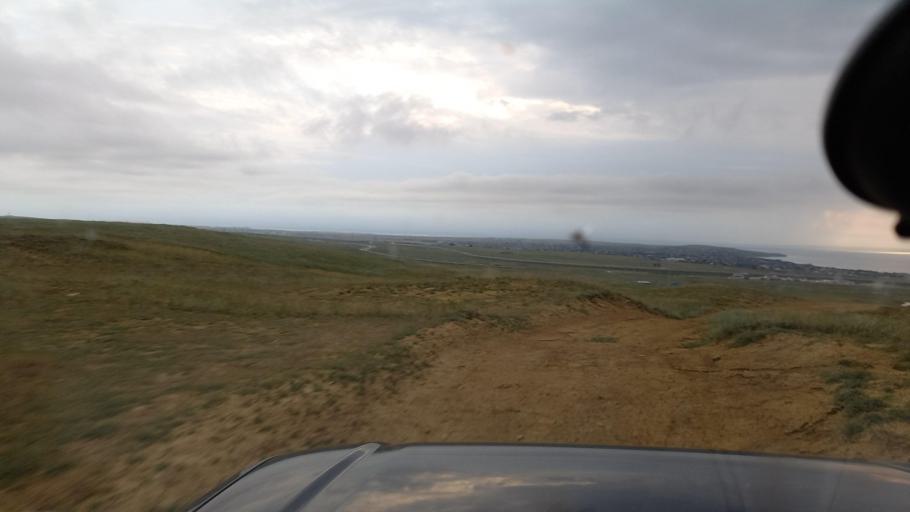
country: RU
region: Krasnodarskiy
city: Taman'
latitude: 45.2058
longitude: 36.7819
